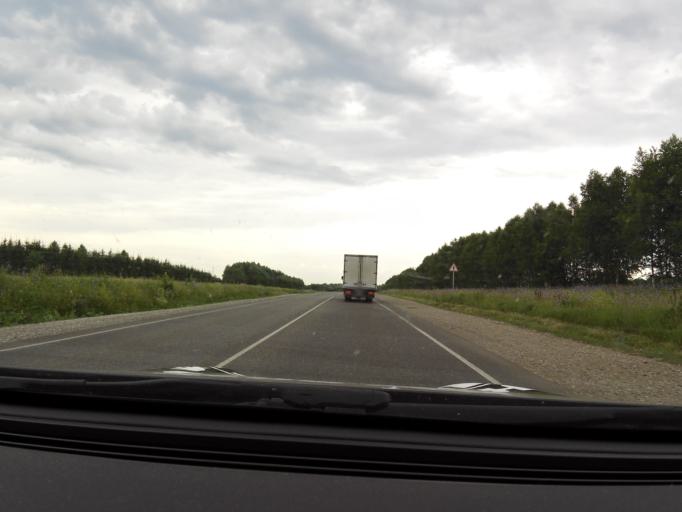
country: RU
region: Bashkortostan
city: Kudeyevskiy
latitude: 54.8102
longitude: 56.6526
